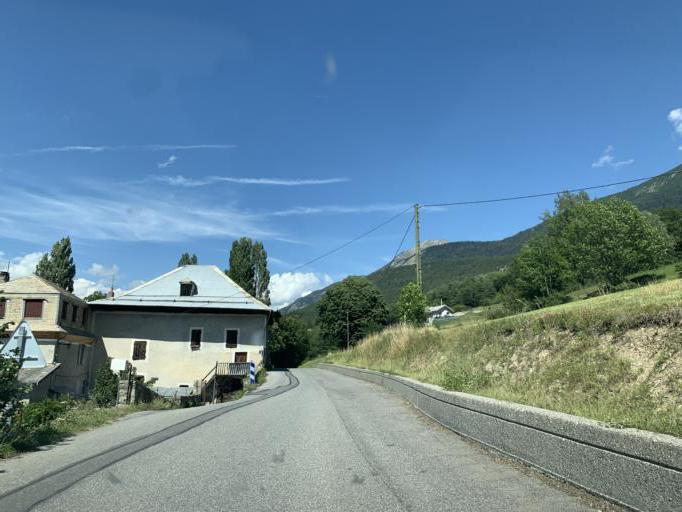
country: FR
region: Provence-Alpes-Cote d'Azur
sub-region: Departement des Hautes-Alpes
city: Embrun
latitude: 44.5789
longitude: 6.5269
